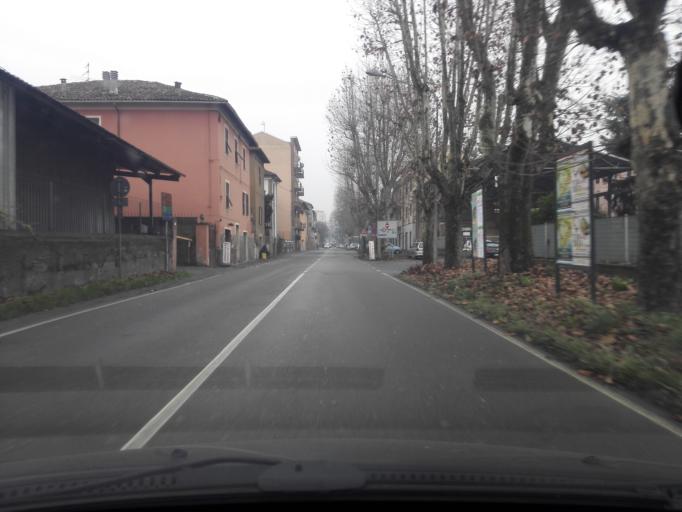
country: IT
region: Piedmont
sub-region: Provincia di Alessandria
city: Novi Ligure
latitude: 44.7673
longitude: 8.7804
